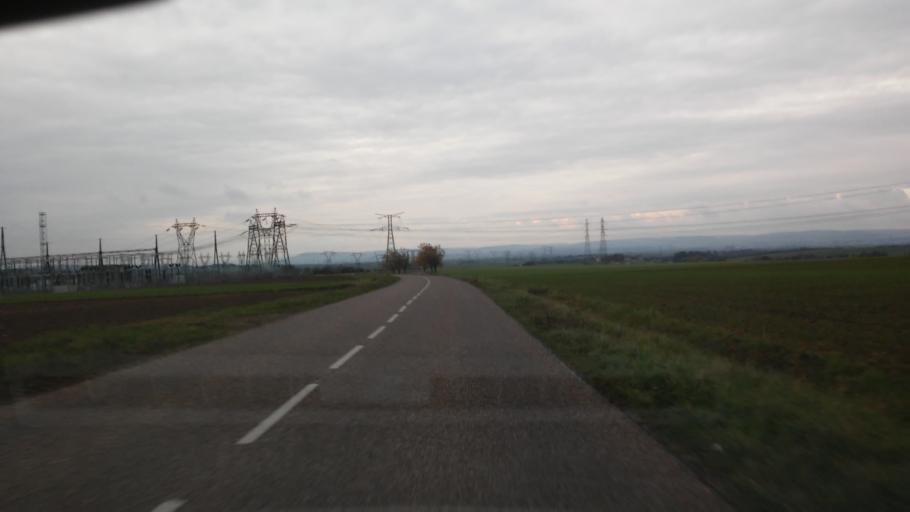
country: FR
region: Lorraine
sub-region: Departement de la Moselle
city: Vigy
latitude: 49.2015
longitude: 6.2797
